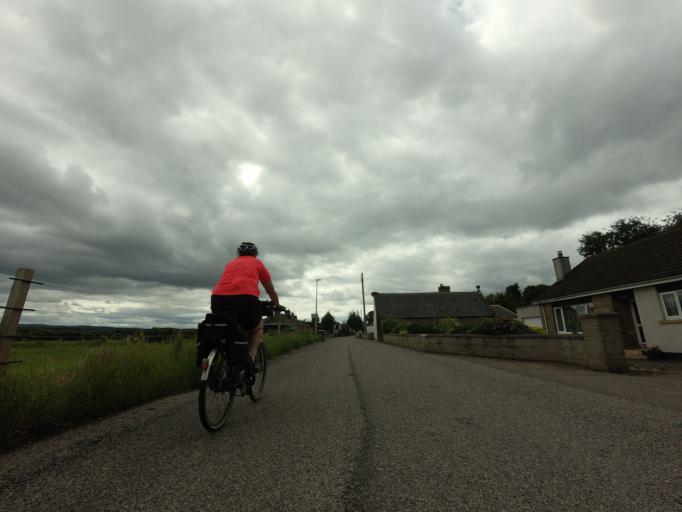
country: GB
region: Scotland
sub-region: Moray
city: Forres
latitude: 57.6070
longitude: -3.6916
